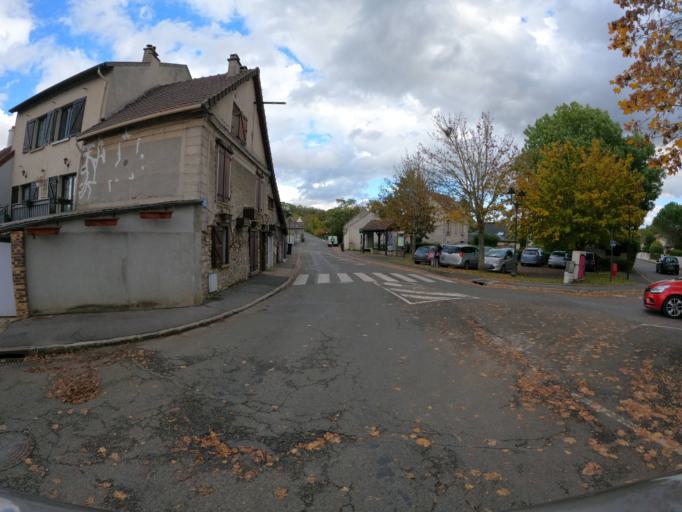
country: FR
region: Ile-de-France
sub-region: Departement de Seine-et-Marne
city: Coupvray
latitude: 48.8970
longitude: 2.7913
